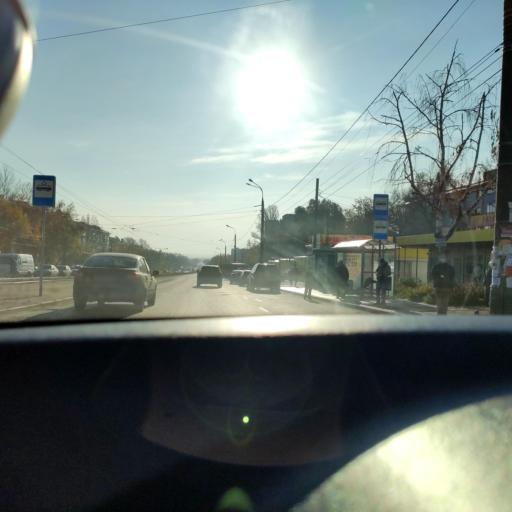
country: RU
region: Samara
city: Samara
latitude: 53.2118
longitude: 50.2284
